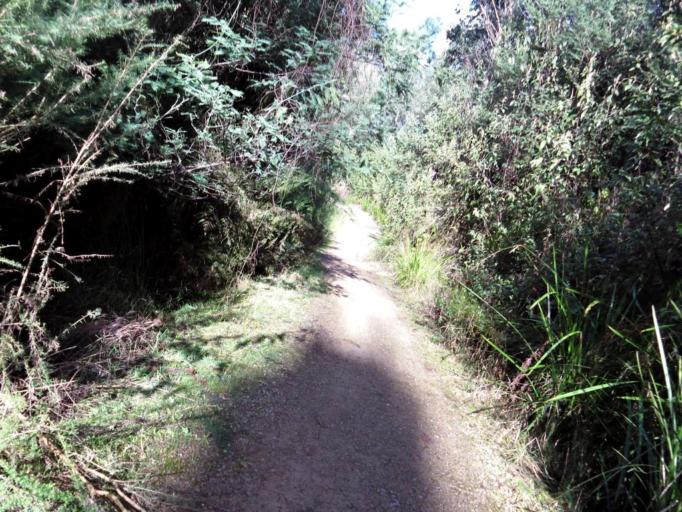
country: AU
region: Victoria
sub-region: Yarra Ranges
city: Millgrove
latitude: -37.5253
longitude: 145.7729
